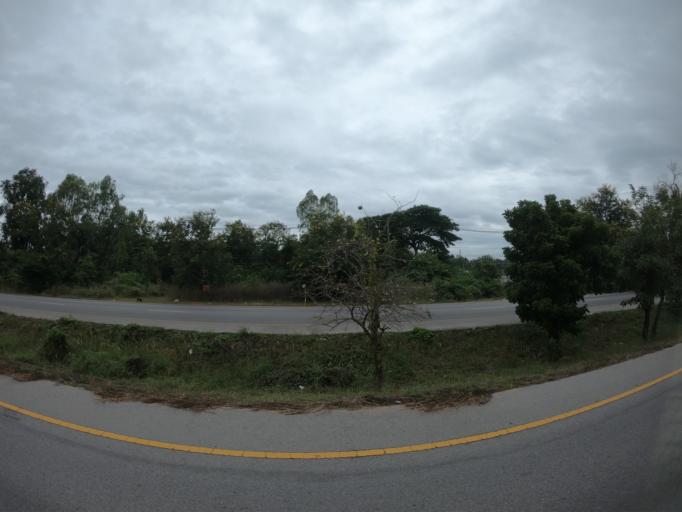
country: TH
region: Kalasin
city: Khong Chai
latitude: 16.1442
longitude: 103.4171
